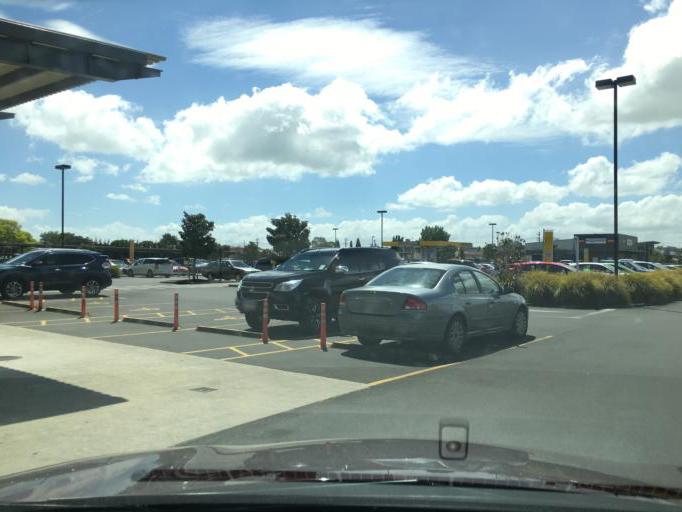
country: NZ
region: Waikato
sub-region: Waipa District
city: Cambridge
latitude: -38.0080
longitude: 175.3403
